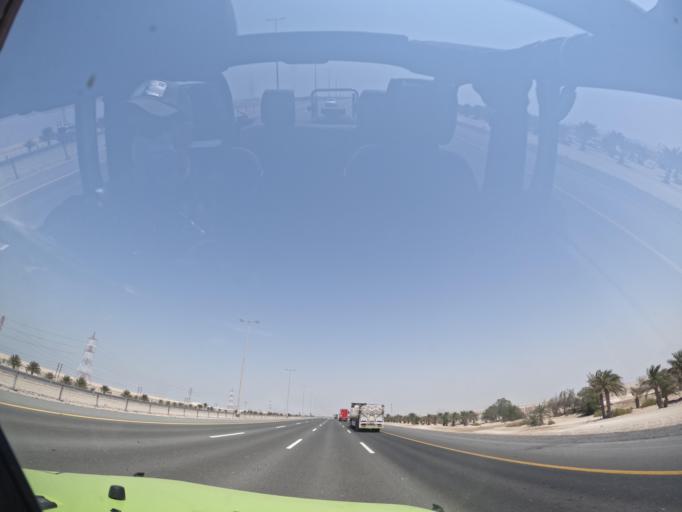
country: AE
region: Abu Dhabi
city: Abu Dhabi
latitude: 24.1986
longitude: 54.3955
